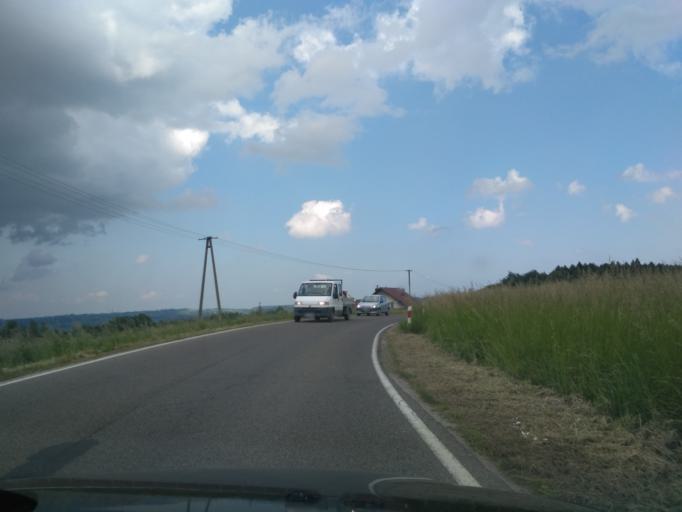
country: PL
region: Subcarpathian Voivodeship
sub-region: Powiat rzeszowski
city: Hyzne
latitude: 49.9384
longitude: 22.1892
